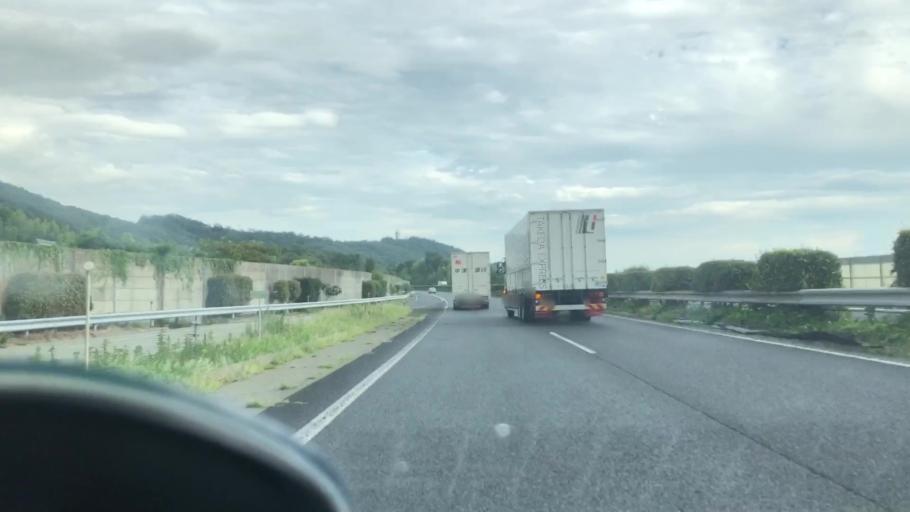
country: JP
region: Hyogo
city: Ono
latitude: 34.9352
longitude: 134.8369
